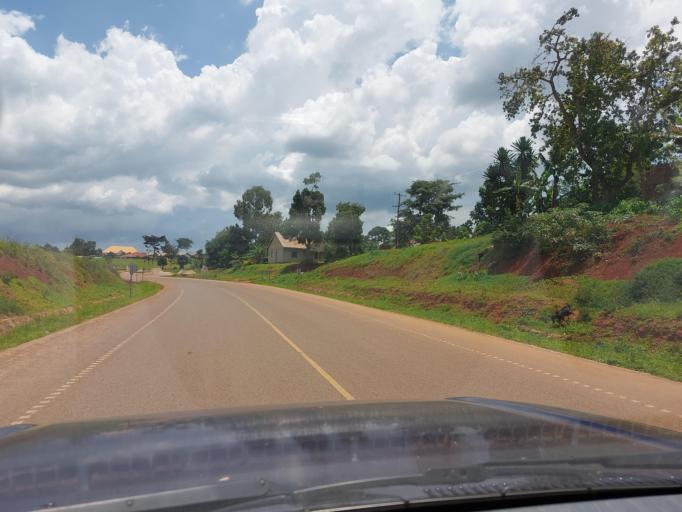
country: UG
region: Central Region
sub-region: Mukono District
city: Mukono
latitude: 0.3046
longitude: 32.7768
